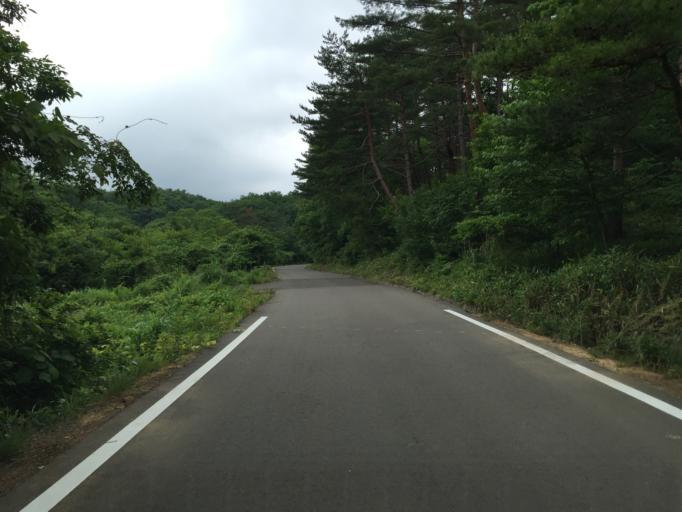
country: JP
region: Miyagi
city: Marumori
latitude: 37.8037
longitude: 140.7507
